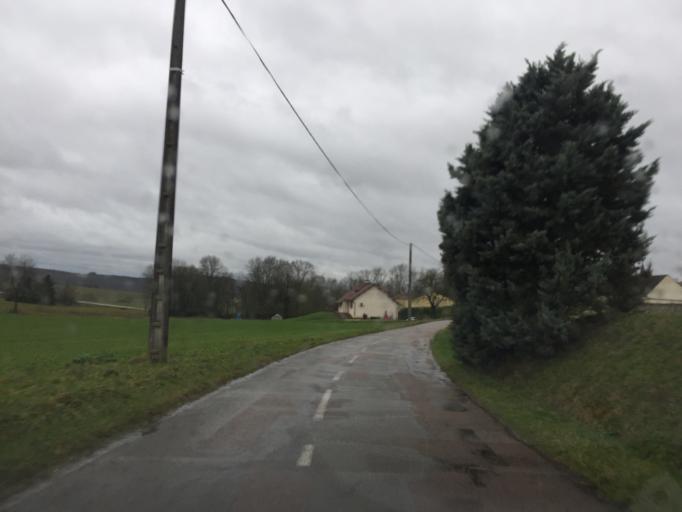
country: FR
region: Franche-Comte
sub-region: Departement du Jura
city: Dole
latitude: 47.1563
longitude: 5.4866
